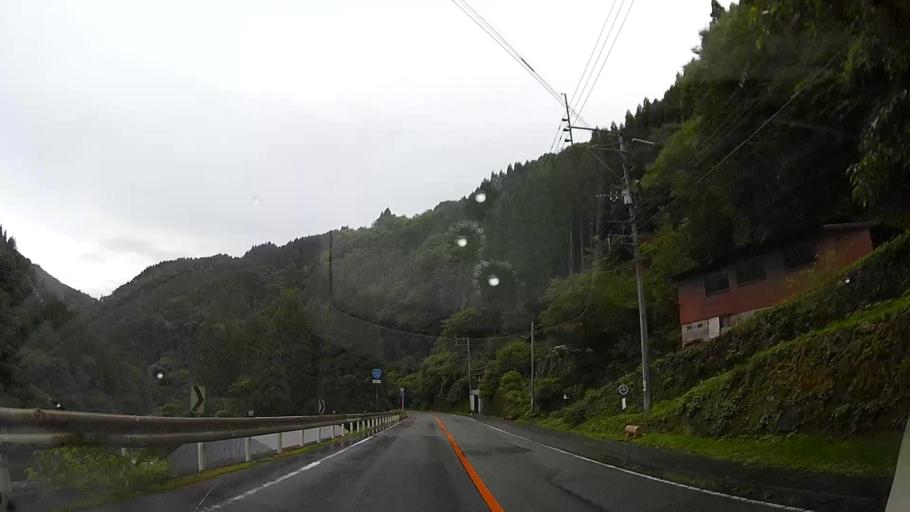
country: JP
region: Oita
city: Tsukawaki
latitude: 33.1661
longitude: 131.0430
